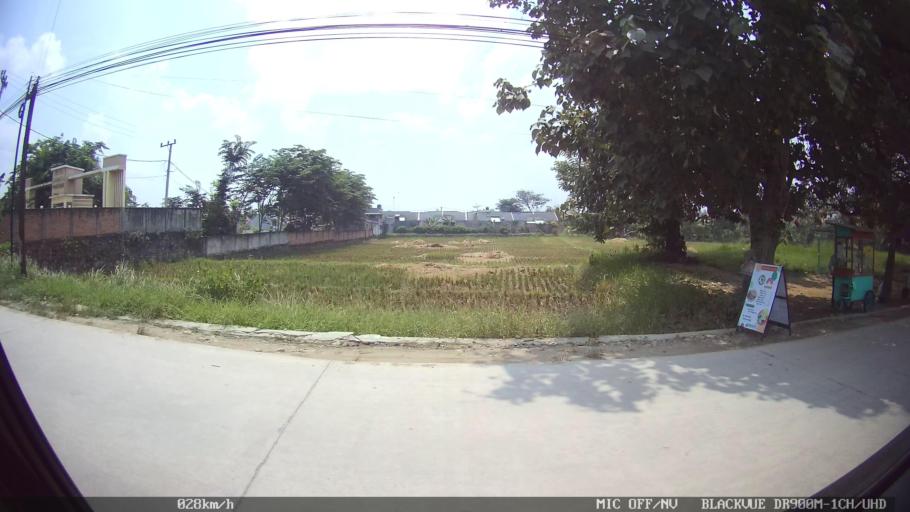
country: ID
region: Lampung
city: Pringsewu
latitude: -5.3416
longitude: 104.9748
